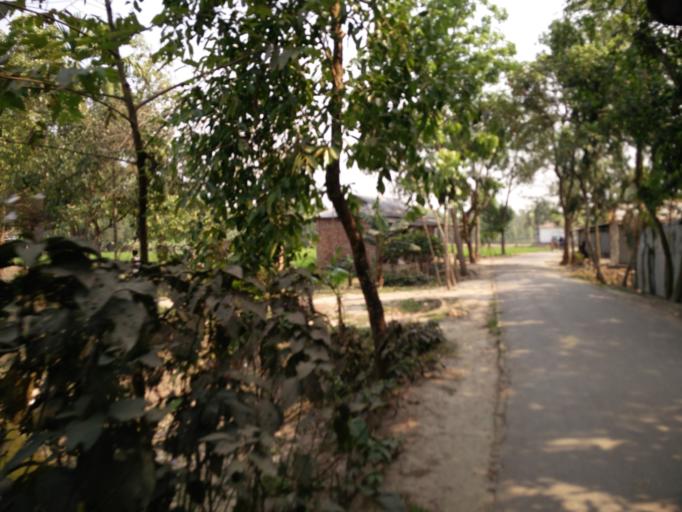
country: BD
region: Dhaka
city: Muktagacha
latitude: 24.9223
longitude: 90.2416
